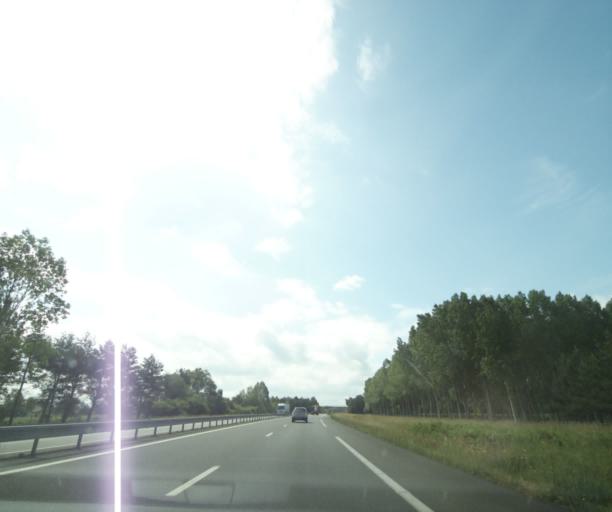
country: FR
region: Pays de la Loire
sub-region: Departement de Maine-et-Loire
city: Jumelles
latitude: 47.4145
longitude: -0.1265
